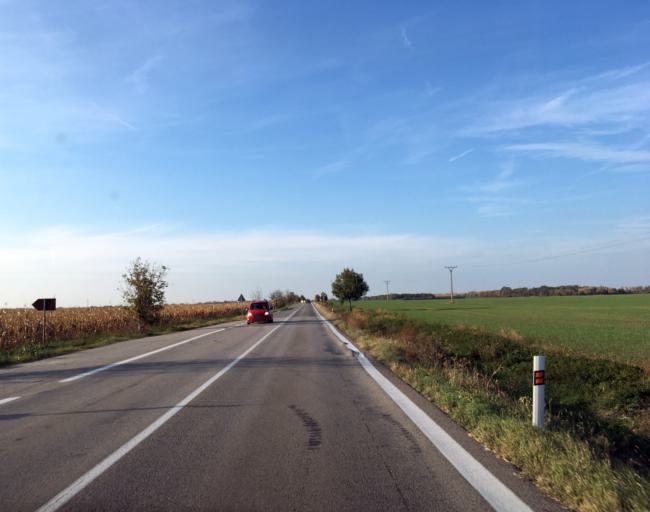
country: SK
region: Nitriansky
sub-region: Okres Nove Zamky
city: Nove Zamky
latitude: 48.0406
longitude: 18.1222
